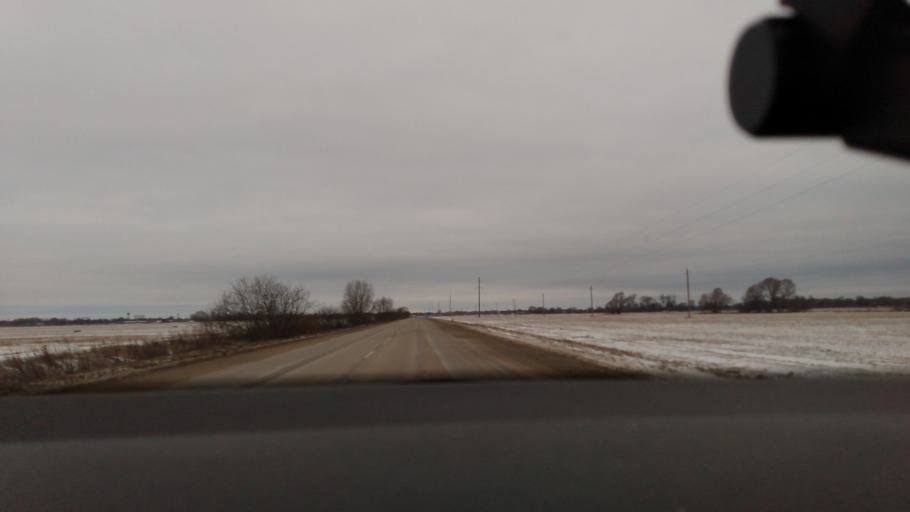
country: RU
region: Moskovskaya
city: Krasnaya Poyma
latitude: 55.0777
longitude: 39.1345
